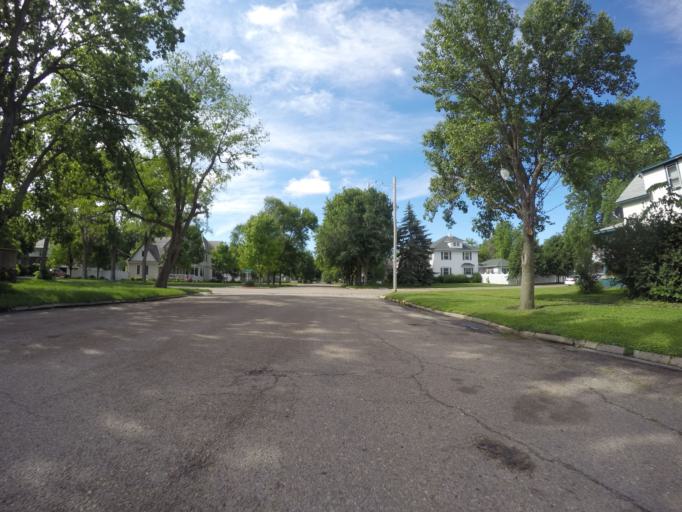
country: US
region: Nebraska
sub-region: Buffalo County
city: Kearney
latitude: 40.6997
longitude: -99.0899
